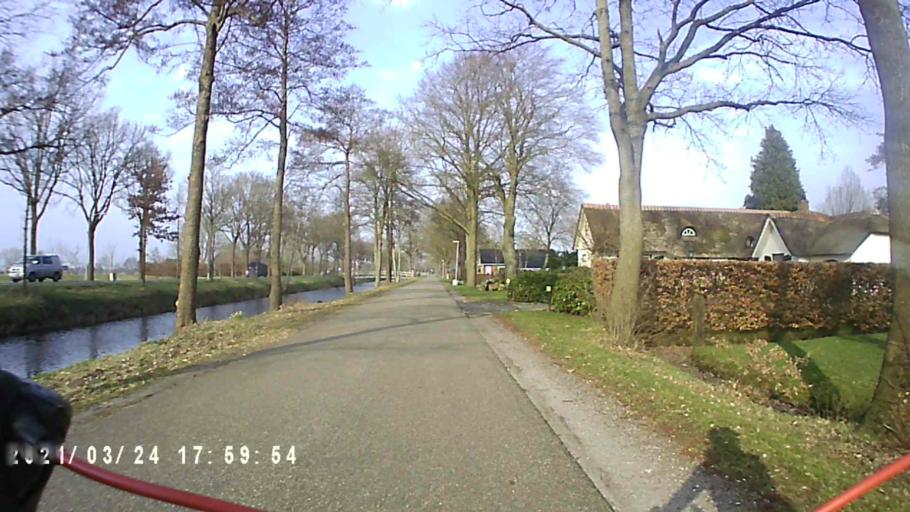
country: NL
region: Groningen
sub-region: Gemeente Leek
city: Leek
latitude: 53.1323
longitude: 6.3567
